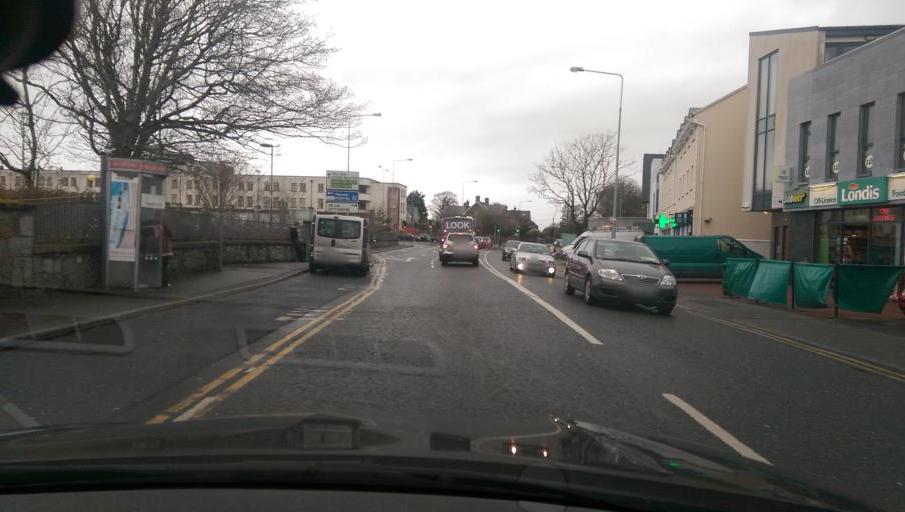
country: IE
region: Connaught
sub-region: County Galway
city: Gaillimh
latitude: 53.2761
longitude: -9.0635
